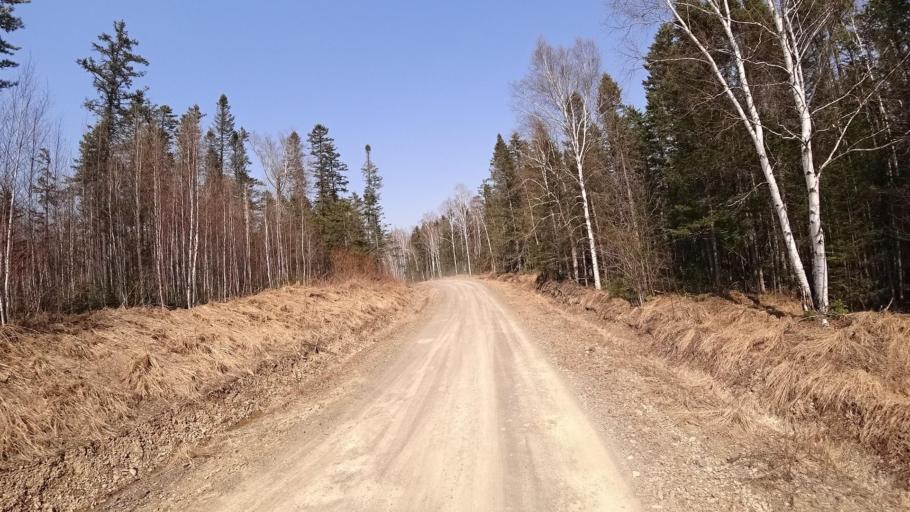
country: RU
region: Khabarovsk Krai
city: Selikhino
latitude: 50.6269
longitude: 137.4054
